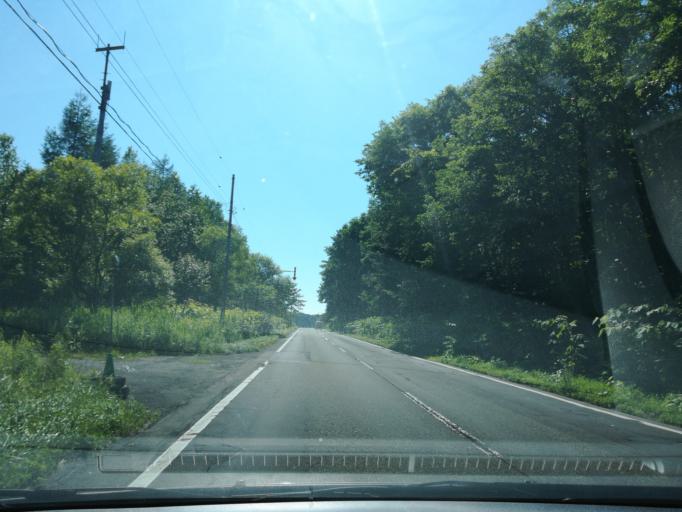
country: JP
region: Hokkaido
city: Chitose
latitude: 42.9094
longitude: 141.9372
